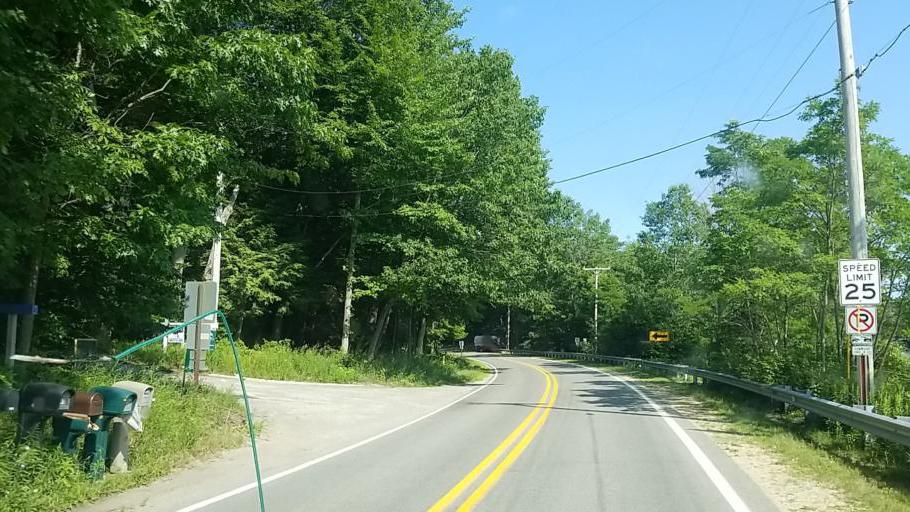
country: US
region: Michigan
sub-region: Muskegon County
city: Whitehall
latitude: 43.3380
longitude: -86.4007
